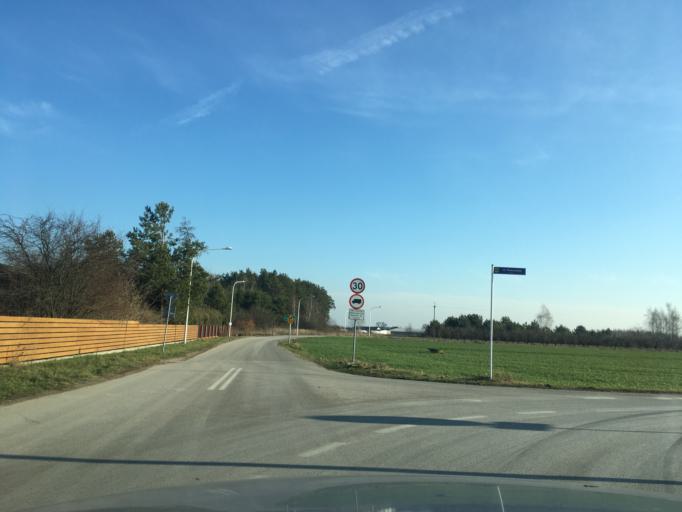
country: PL
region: Masovian Voivodeship
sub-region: Powiat pruszkowski
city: Nadarzyn
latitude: 52.0424
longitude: 20.8275
